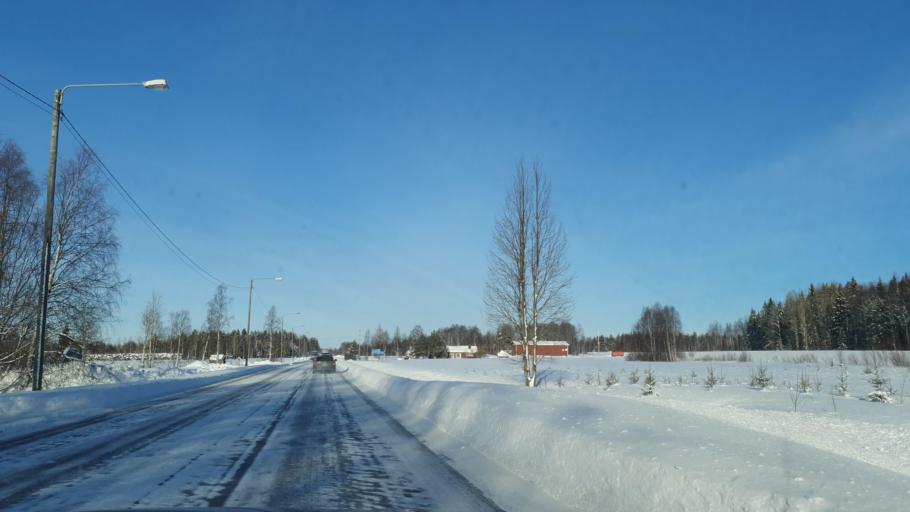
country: FI
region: Lapland
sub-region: Torniolaakso
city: Ylitornio
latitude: 66.1192
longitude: 23.9493
